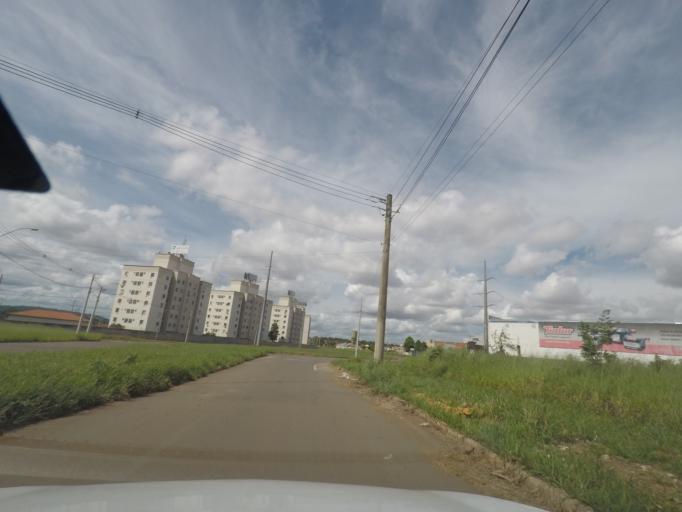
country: BR
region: Goias
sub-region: Goiania
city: Goiania
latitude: -16.7214
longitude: -49.3499
